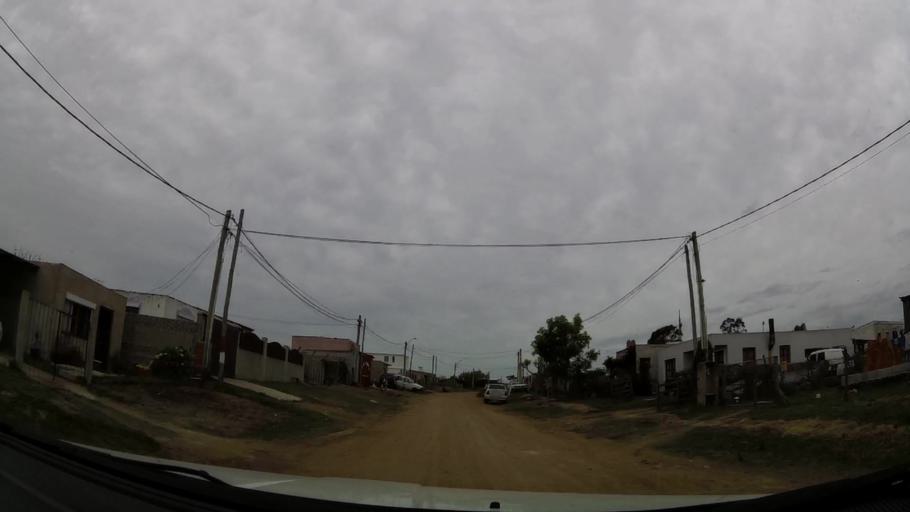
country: UY
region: Maldonado
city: Maldonado
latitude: -34.8821
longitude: -54.9407
